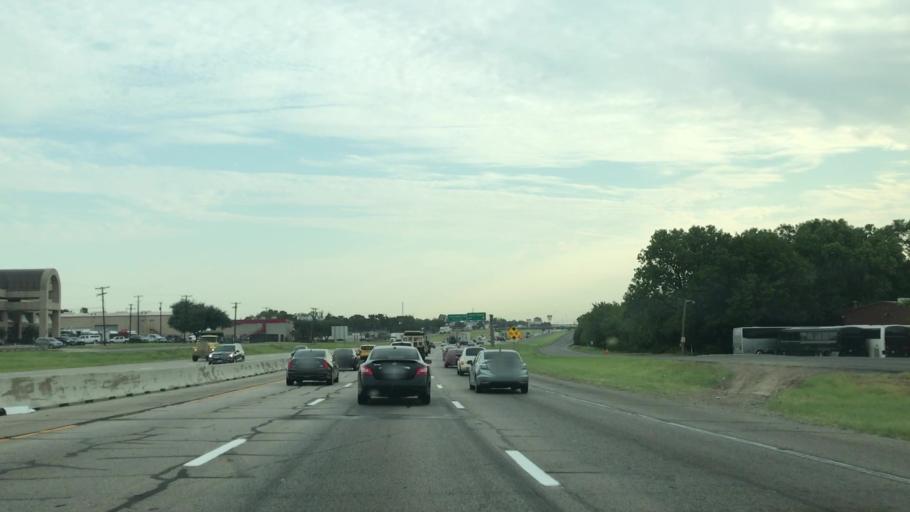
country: US
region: Texas
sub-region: Dallas County
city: Irving
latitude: 32.8176
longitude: -96.9215
